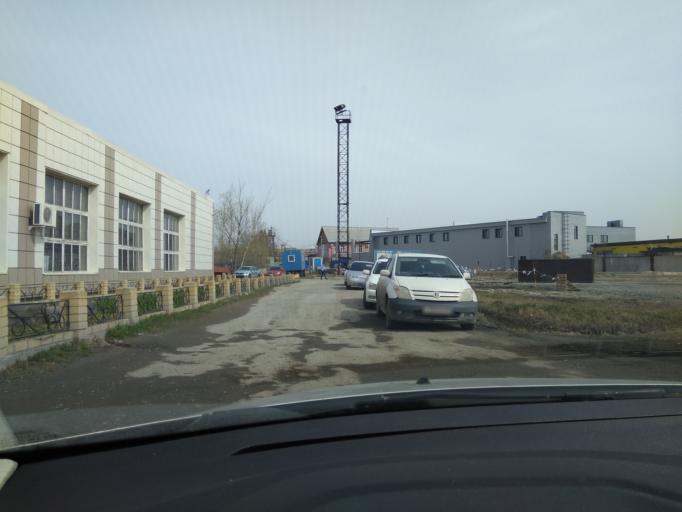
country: RU
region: Tjumen
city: Melioratorov
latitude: 57.1897
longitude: 65.5990
